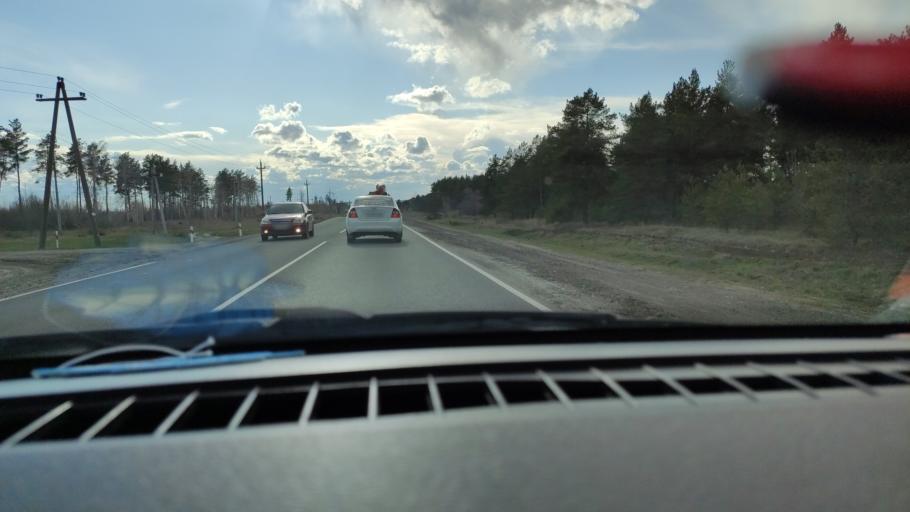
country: RU
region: Saratov
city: Sennoy
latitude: 52.1452
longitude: 46.9363
